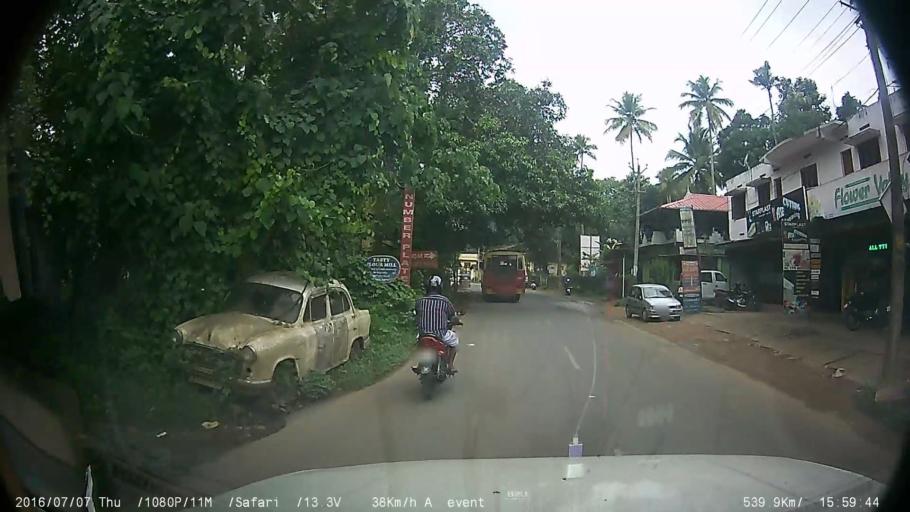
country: IN
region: Kerala
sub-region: Ernakulam
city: Piravam
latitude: 9.8561
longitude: 76.5964
